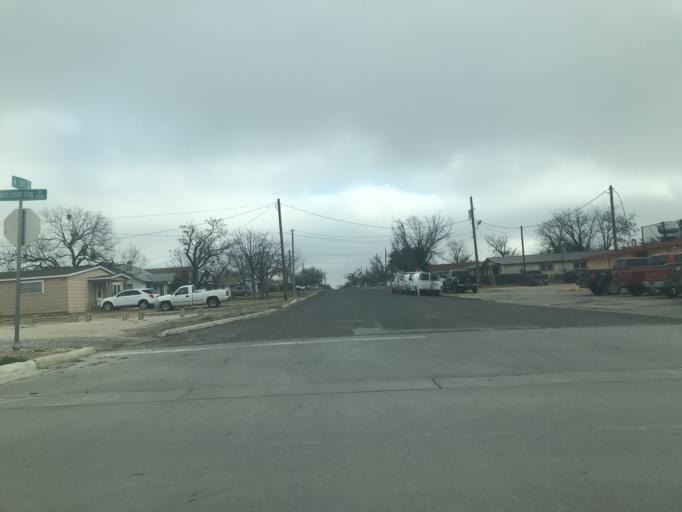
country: US
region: Texas
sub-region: Tom Green County
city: San Angelo
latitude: 31.4815
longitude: -100.4542
